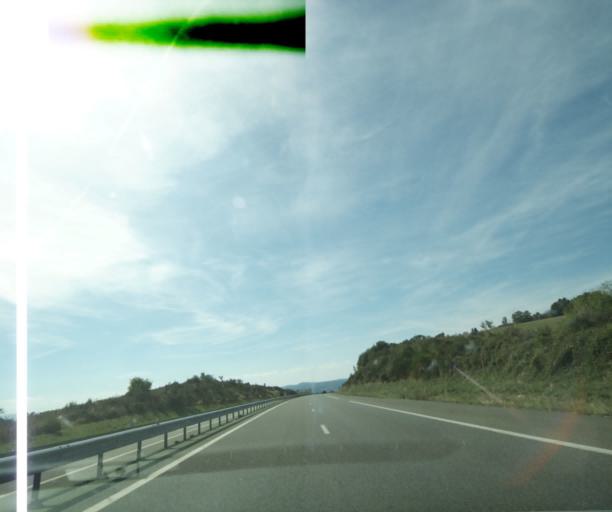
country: FR
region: Auvergne
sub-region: Departement du Puy-de-Dome
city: Saint-Ours
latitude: 45.8723
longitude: 2.9026
